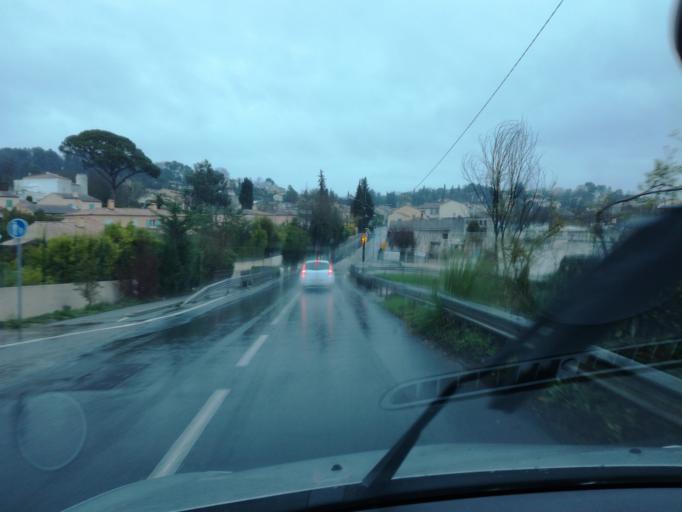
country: FR
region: Provence-Alpes-Cote d'Azur
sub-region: Departement des Alpes-Maritimes
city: Valbonne
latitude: 43.6424
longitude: 7.0034
